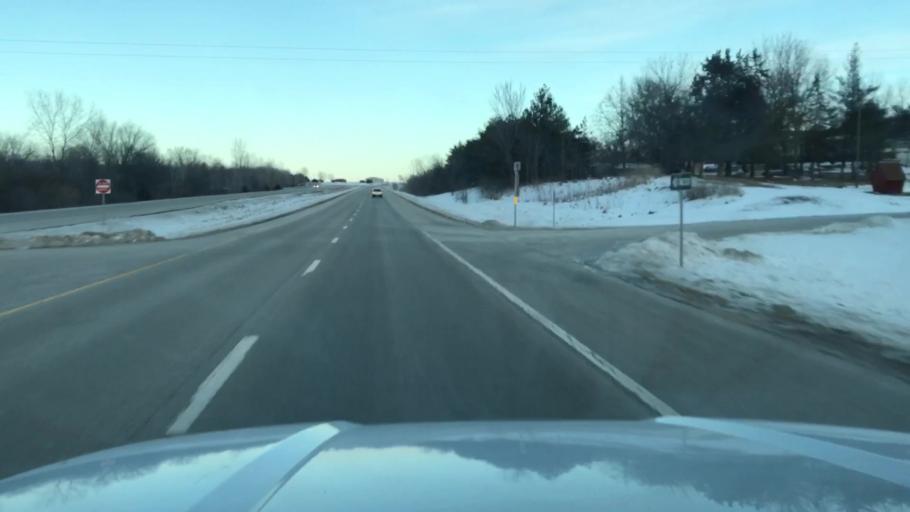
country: US
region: Missouri
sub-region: Clinton County
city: Gower
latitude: 39.7575
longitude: -94.5776
